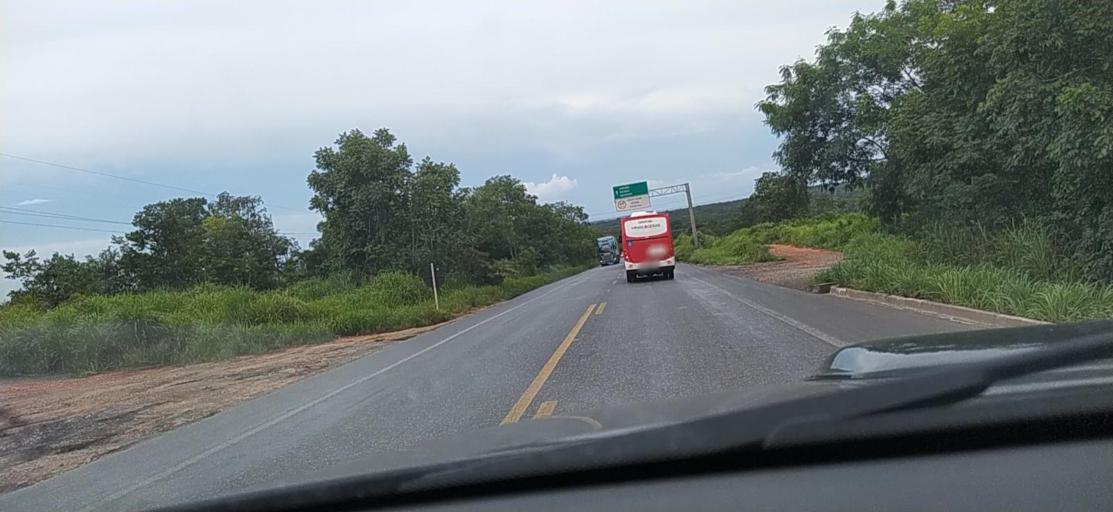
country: BR
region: Minas Gerais
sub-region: Montes Claros
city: Montes Claros
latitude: -16.6675
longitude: -43.7879
